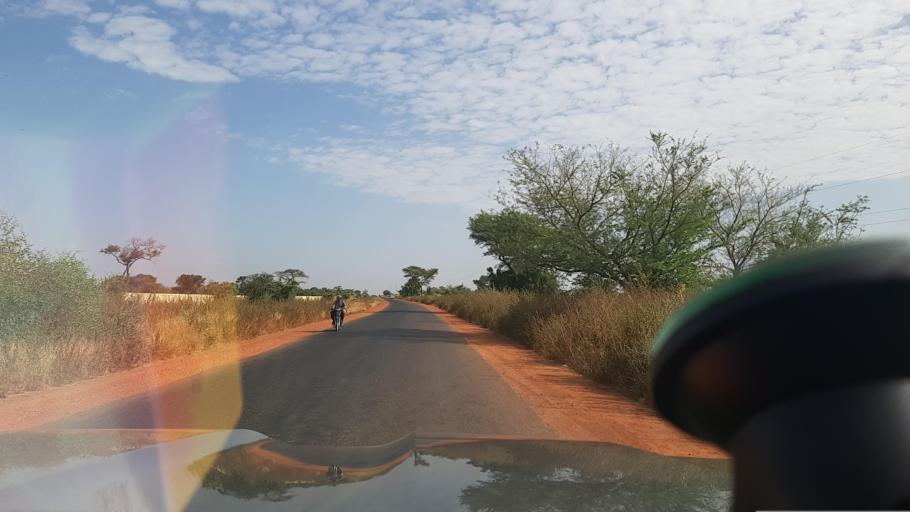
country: ML
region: Segou
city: Segou
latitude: 13.5319
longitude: -6.1263
